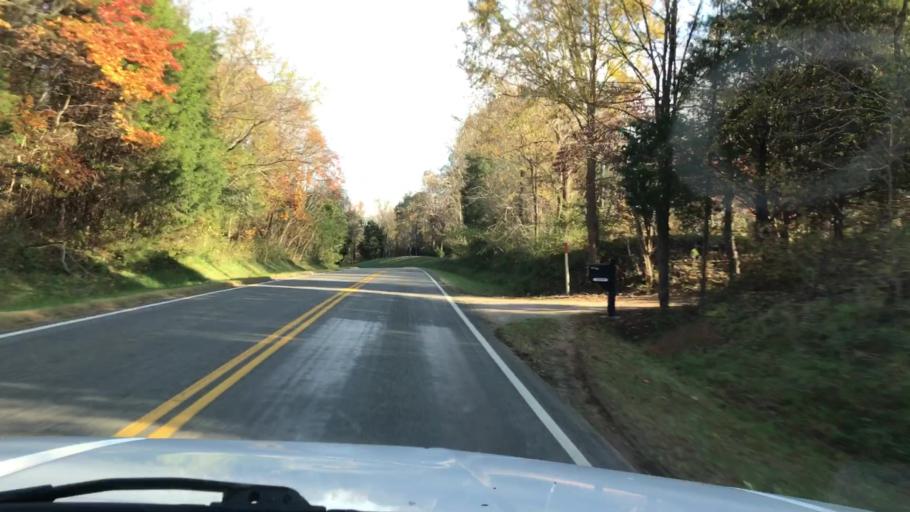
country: US
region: Virginia
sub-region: Goochland County
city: Goochland
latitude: 37.6644
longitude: -77.8721
